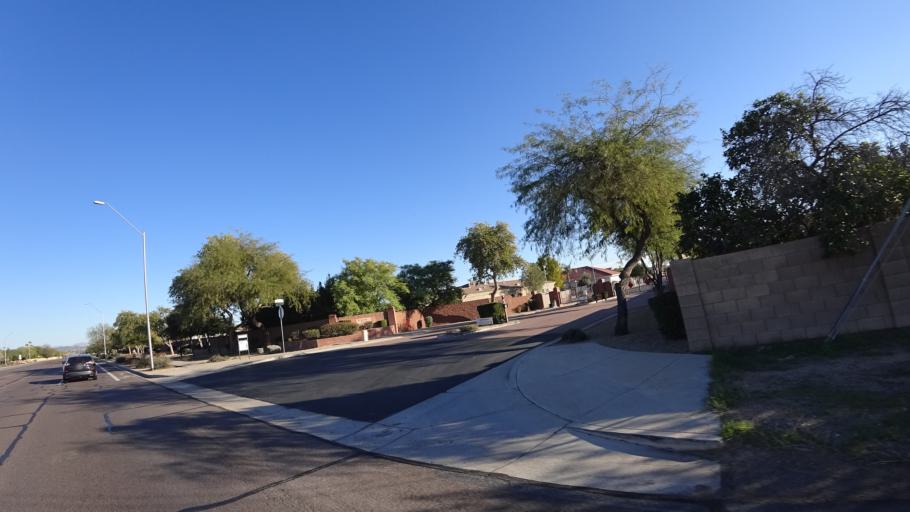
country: US
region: Arizona
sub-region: Maricopa County
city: Peoria
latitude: 33.7125
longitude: -112.1640
